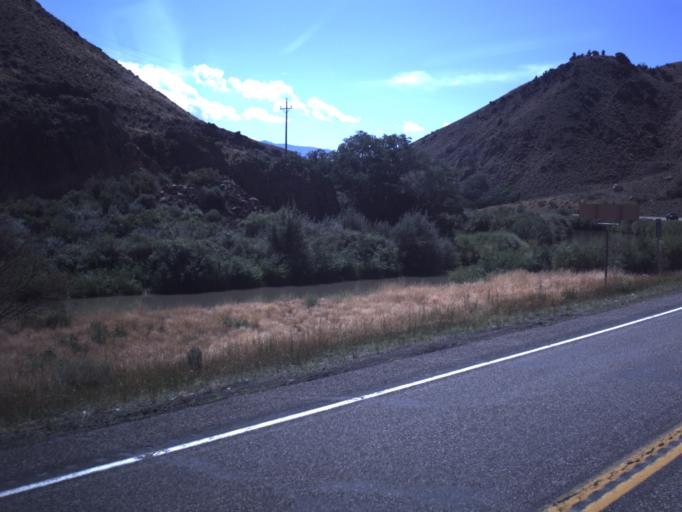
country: US
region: Utah
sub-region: Sevier County
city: Monroe
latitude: 38.4987
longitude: -112.2570
